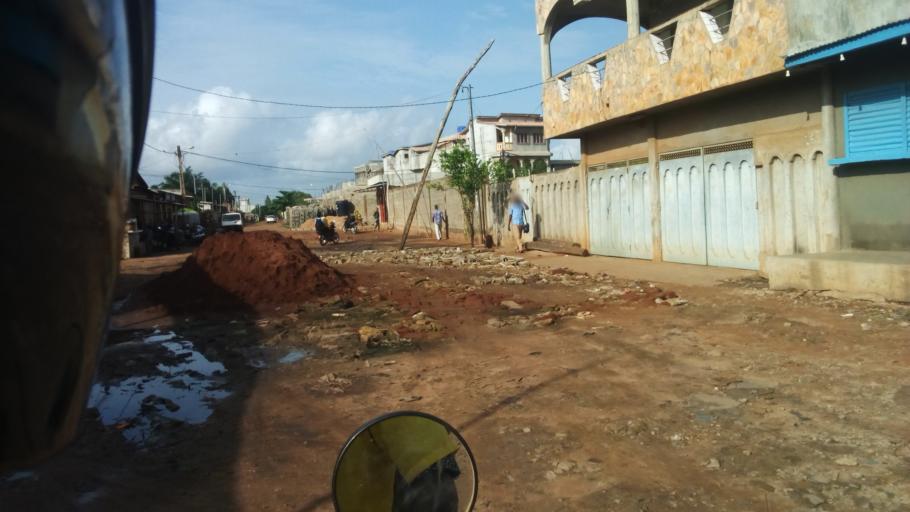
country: BJ
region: Atlantique
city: Abomey-Calavi
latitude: 6.4327
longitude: 2.3416
